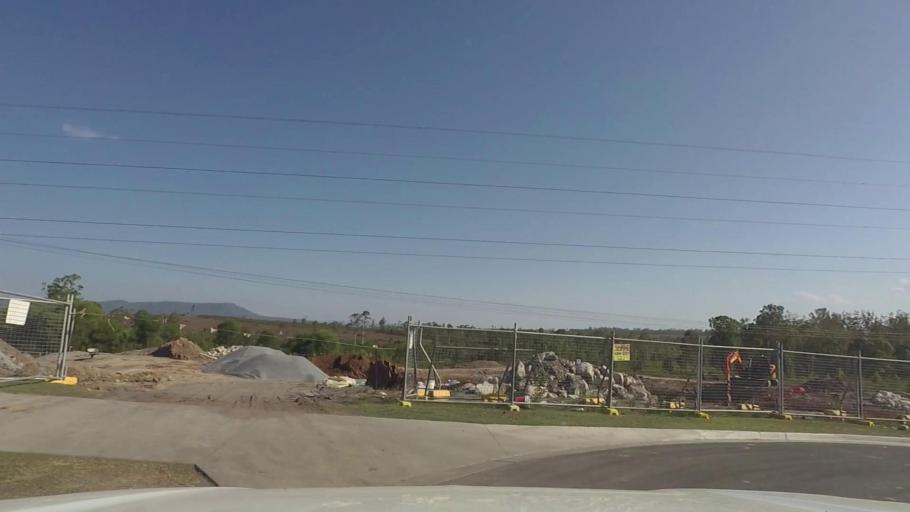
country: AU
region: Queensland
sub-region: Logan
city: Chambers Flat
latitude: -27.8183
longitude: 153.1297
